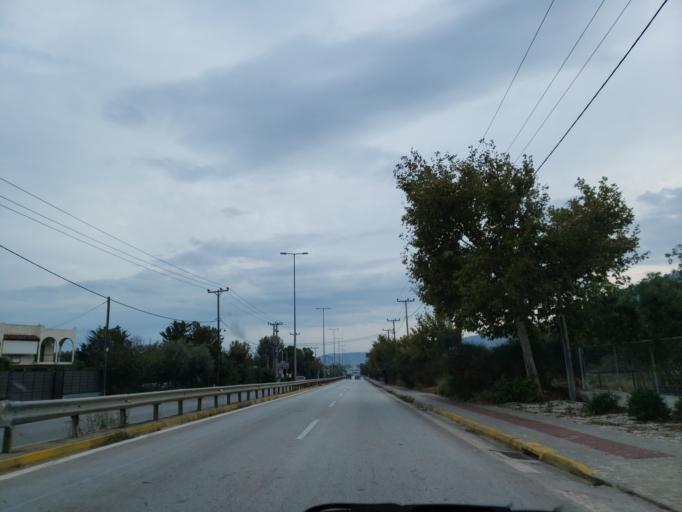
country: GR
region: Attica
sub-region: Nomarchia Anatolikis Attikis
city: Aghios Panteleimon
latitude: 38.1109
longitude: 23.9697
